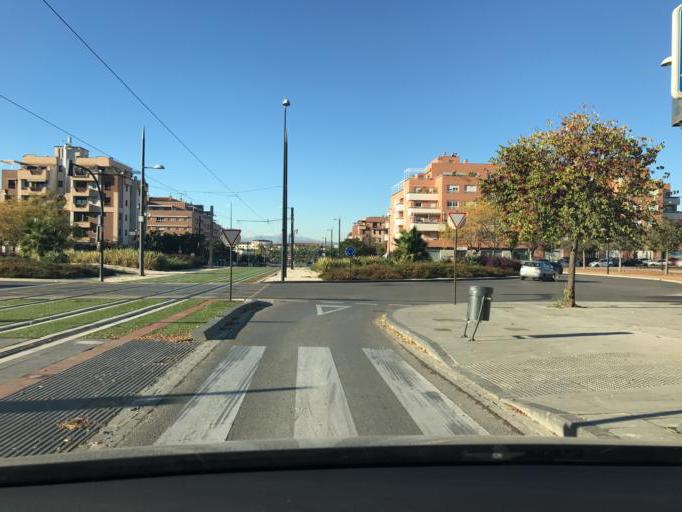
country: ES
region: Andalusia
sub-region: Provincia de Granada
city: Maracena
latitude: 37.2033
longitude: -3.6201
